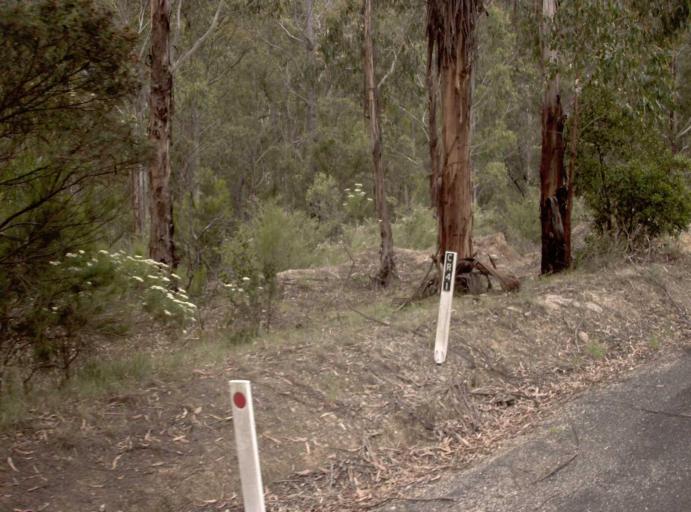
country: AU
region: New South Wales
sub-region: Bombala
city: Bombala
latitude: -37.2485
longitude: 149.2534
